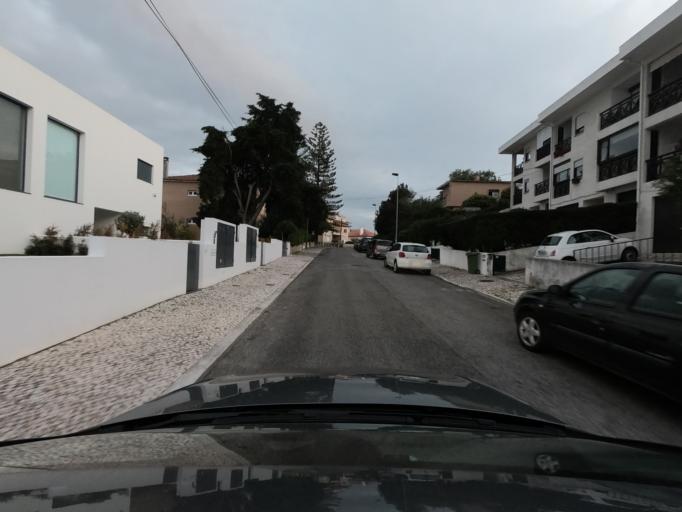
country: PT
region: Lisbon
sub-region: Oeiras
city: Terrugem
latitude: 38.7036
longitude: -9.2756
